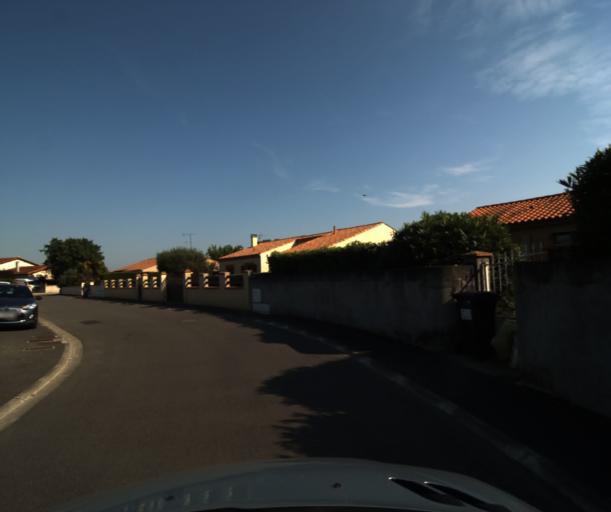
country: FR
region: Midi-Pyrenees
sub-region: Departement de la Haute-Garonne
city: Labarthe-sur-Leze
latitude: 43.4770
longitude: 1.3924
